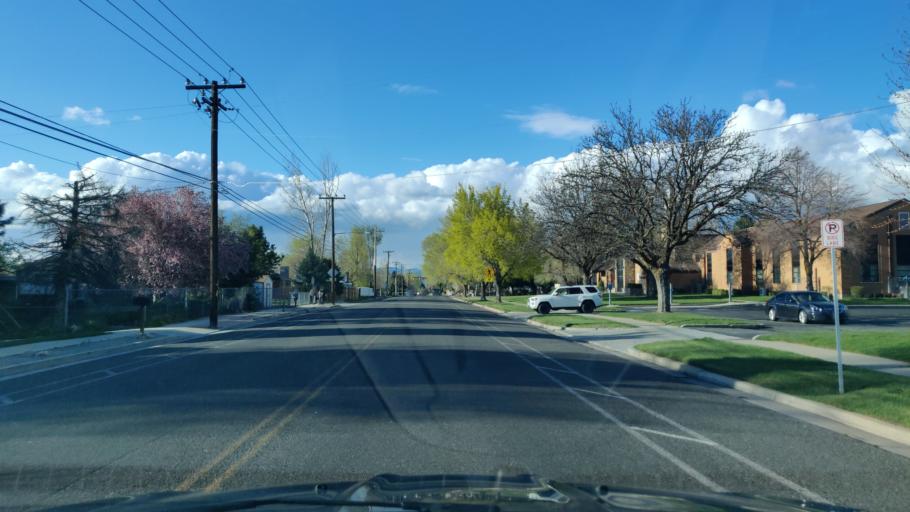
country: US
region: Utah
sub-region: Salt Lake County
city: Cottonwood Heights
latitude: 40.6358
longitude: -111.8247
